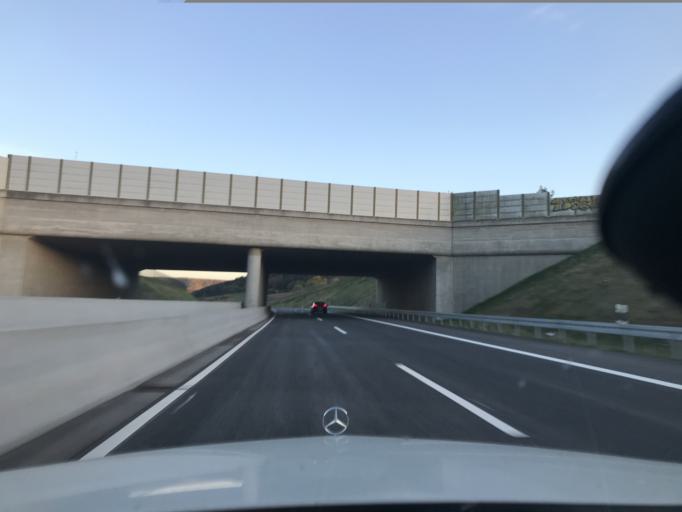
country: DE
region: Hesse
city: Waldkappel
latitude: 51.1593
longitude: 9.8532
